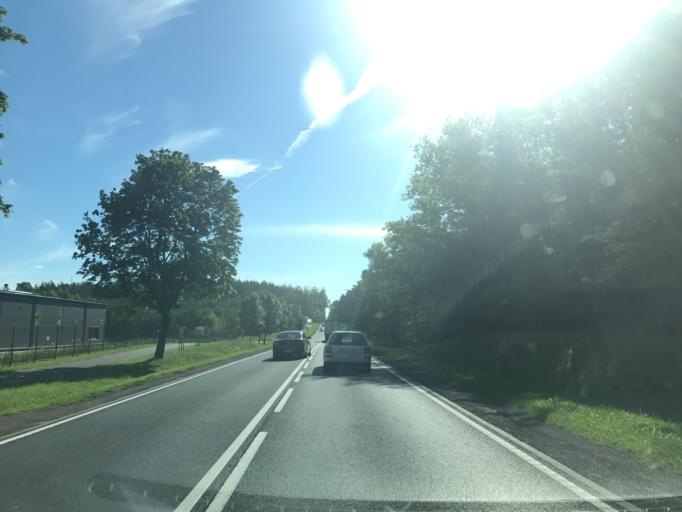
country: PL
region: Pomeranian Voivodeship
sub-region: Powiat czluchowski
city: Czluchow
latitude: 53.6855
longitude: 17.4350
